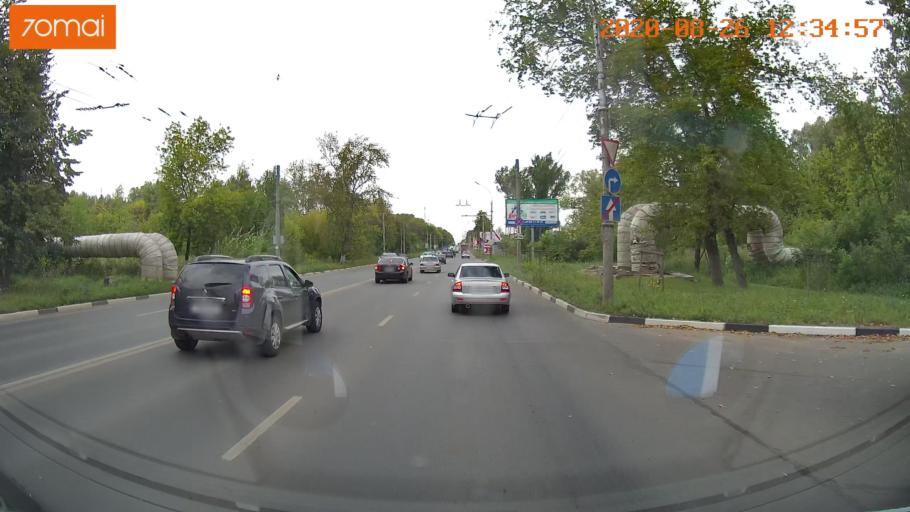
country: RU
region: Rjazan
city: Ryazan'
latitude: 54.5919
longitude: 39.7699
